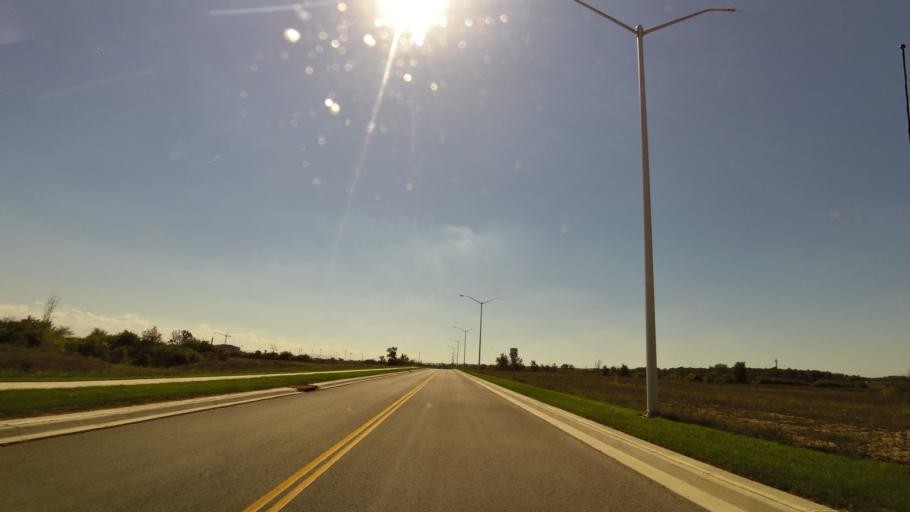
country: CA
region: Ontario
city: Burlington
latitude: 43.4466
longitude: -79.7723
